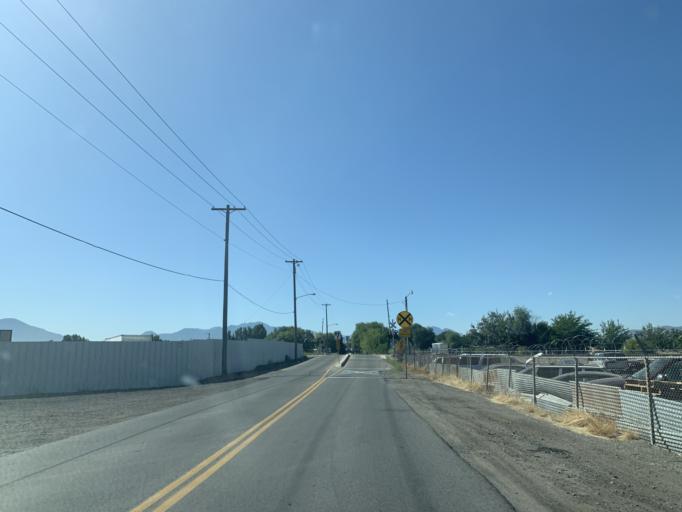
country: US
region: Utah
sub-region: Utah County
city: Orem
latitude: 40.2604
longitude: -111.7083
